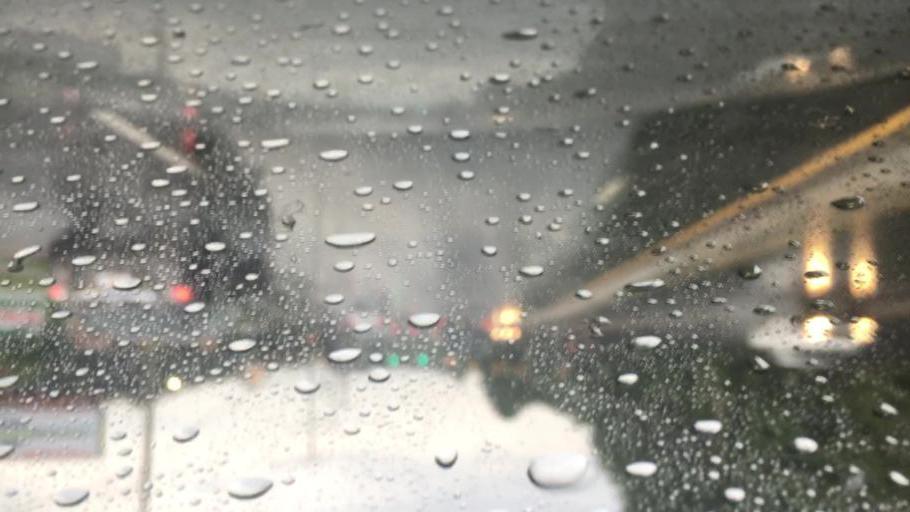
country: US
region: North Carolina
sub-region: Cumberland County
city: Fort Bragg
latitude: 35.0658
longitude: -79.0136
